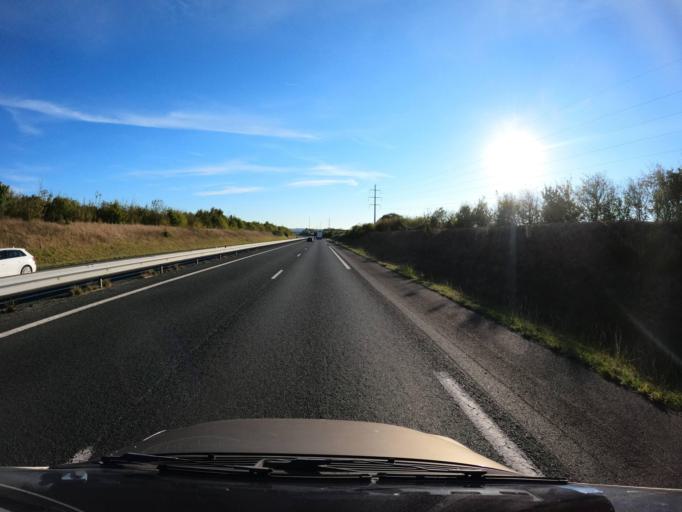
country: FR
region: Pays de la Loire
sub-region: Departement de Maine-et-Loire
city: Mazieres-en-Mauges
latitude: 47.0556
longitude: -0.8329
